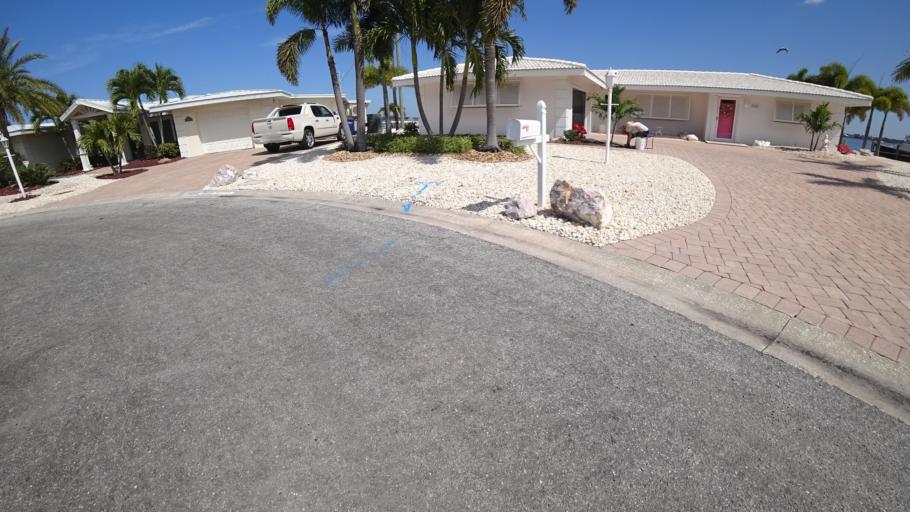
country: US
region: Florida
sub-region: Manatee County
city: Cortez
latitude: 27.4692
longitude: -82.6616
